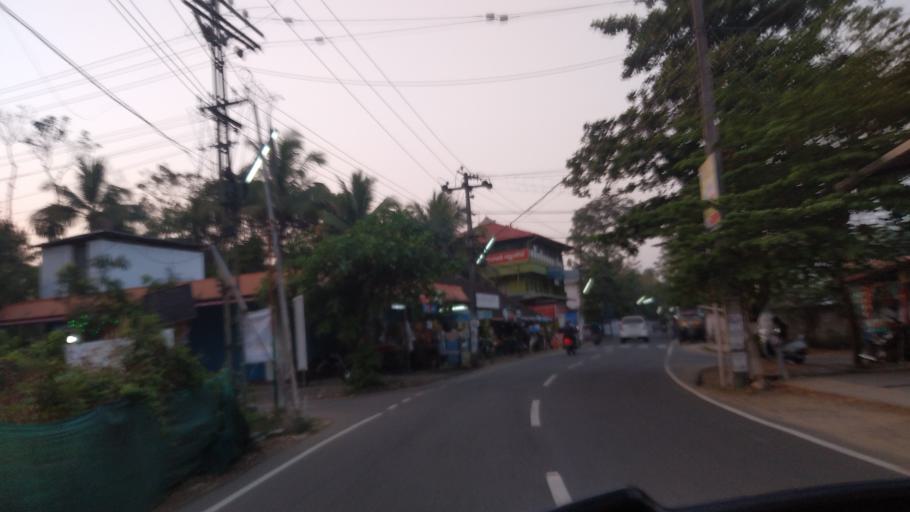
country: IN
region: Kerala
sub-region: Ernakulam
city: Elur
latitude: 10.1307
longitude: 76.2335
